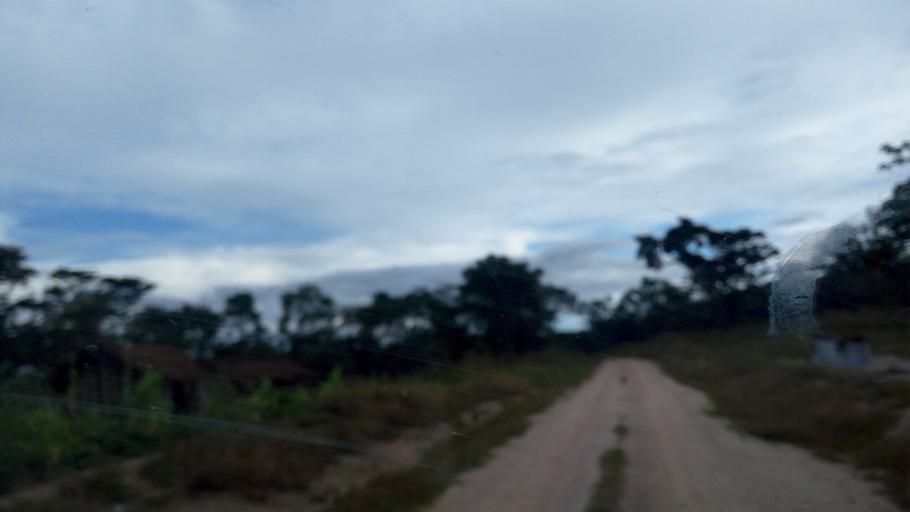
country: CD
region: Katanga
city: Kalemie
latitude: -6.5988
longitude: 29.0415
